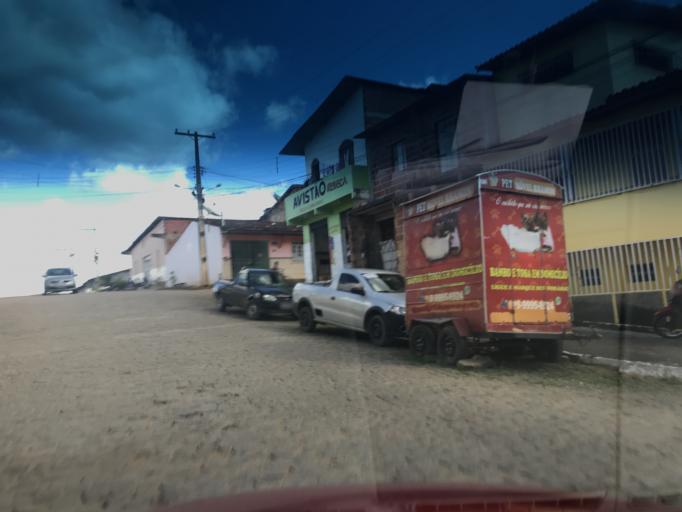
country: BR
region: Bahia
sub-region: Gandu
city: Gandu
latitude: -13.7459
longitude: -39.4945
